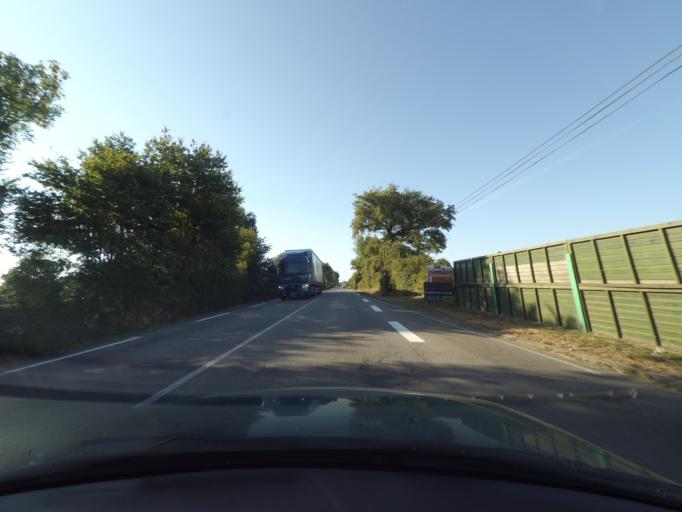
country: FR
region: Poitou-Charentes
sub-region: Departement des Deux-Sevres
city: Chiche
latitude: 46.7530
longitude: -0.3083
